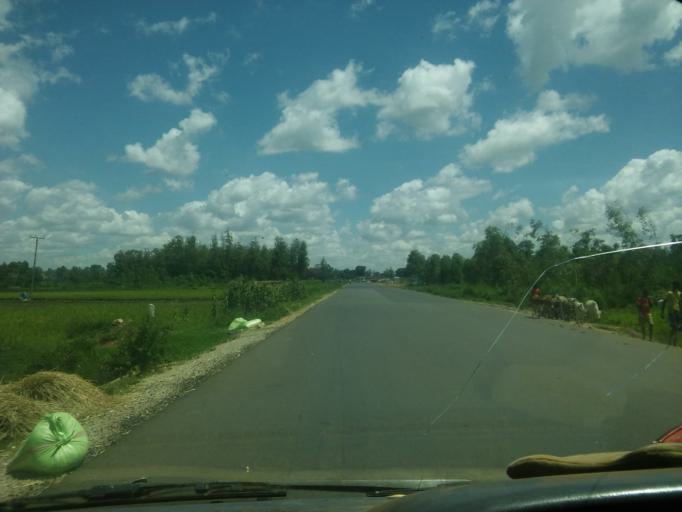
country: UG
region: Eastern Region
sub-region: Mbale District
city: Mbale
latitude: 1.0748
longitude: 34.1274
